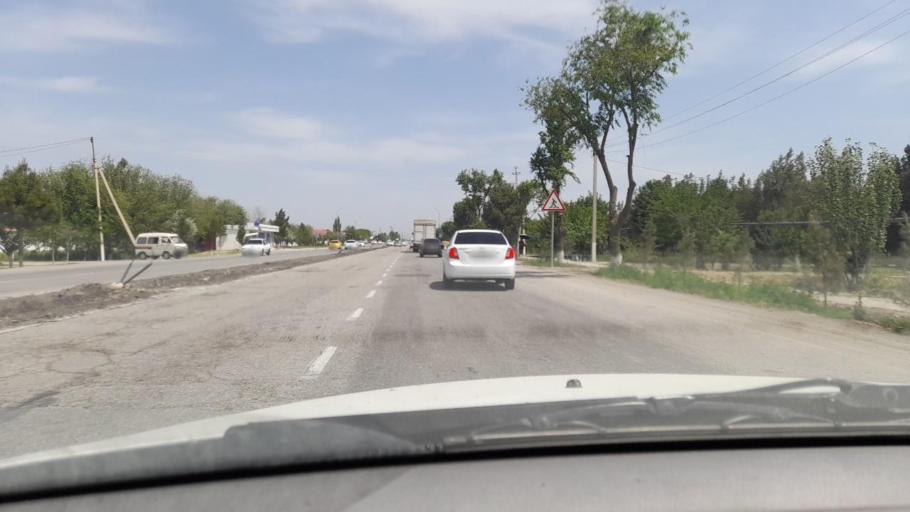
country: UZ
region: Navoiy
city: Beshrabot
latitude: 40.1429
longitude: 65.2966
